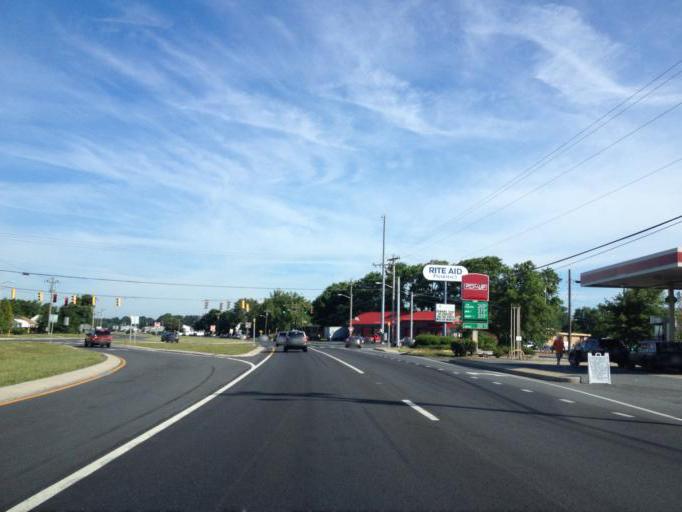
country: US
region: Delaware
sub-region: Sussex County
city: Millsboro
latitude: 38.5850
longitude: -75.2945
